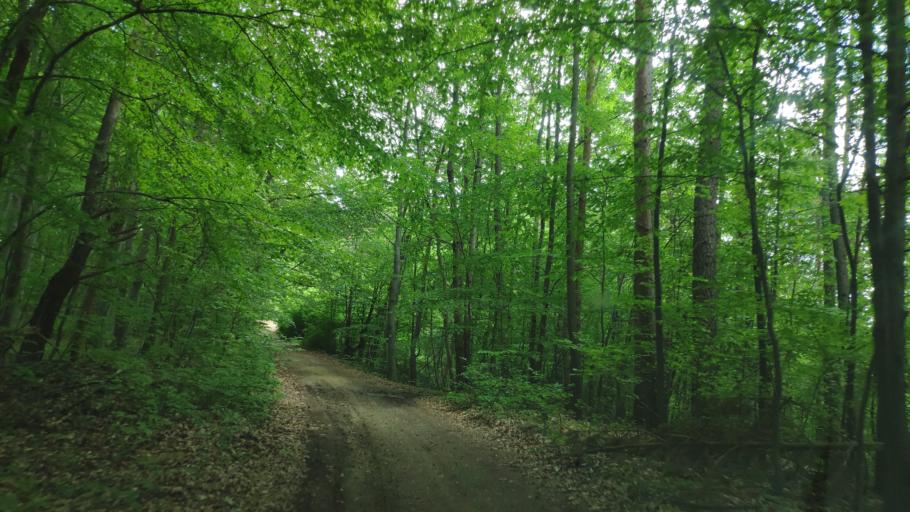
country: SK
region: Presovsky
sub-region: Okres Presov
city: Presov
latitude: 48.9408
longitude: 21.1162
